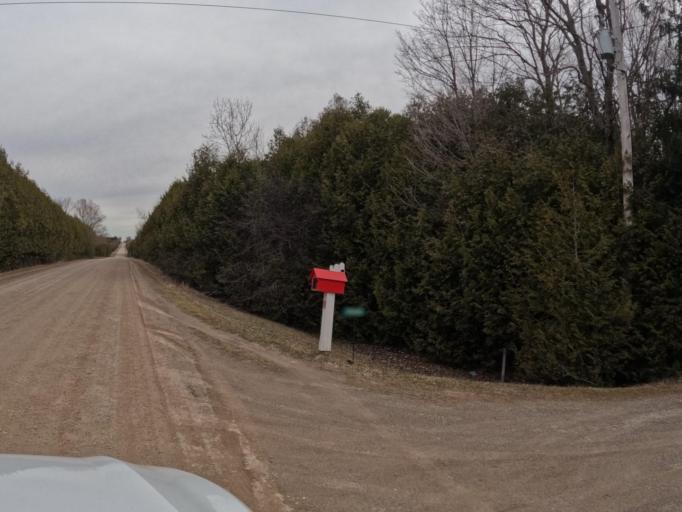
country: CA
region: Ontario
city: Orangeville
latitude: 43.9266
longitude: -80.2569
